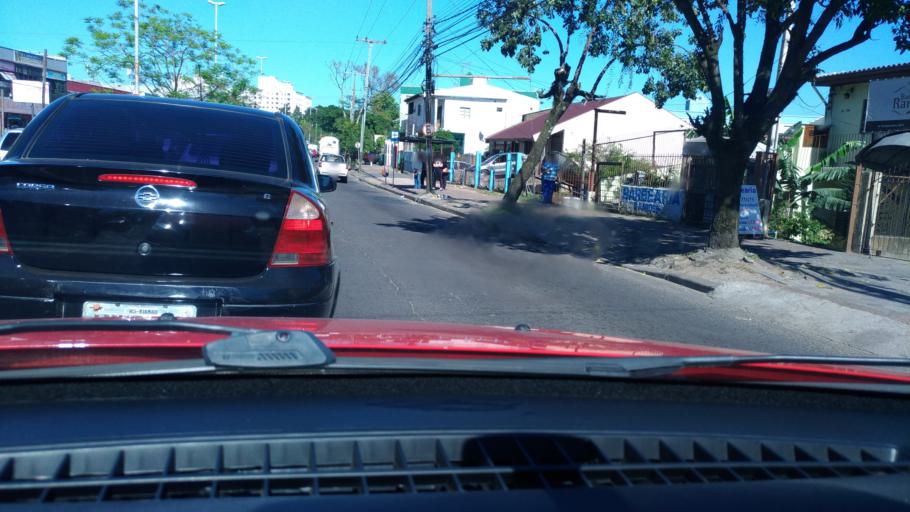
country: BR
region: Rio Grande do Sul
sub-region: Cachoeirinha
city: Cachoeirinha
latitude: -30.0394
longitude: -51.1249
